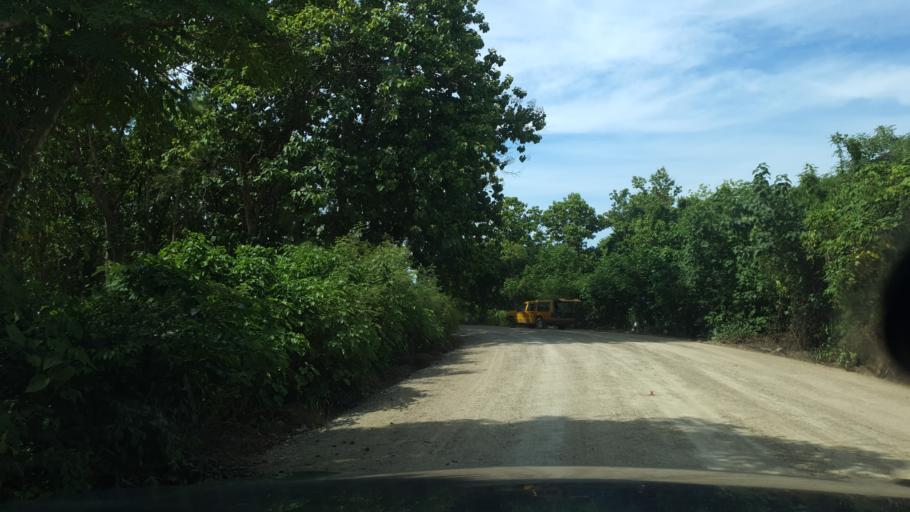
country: TH
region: Sukhothai
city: Si Samrong
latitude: 17.2134
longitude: 99.7181
